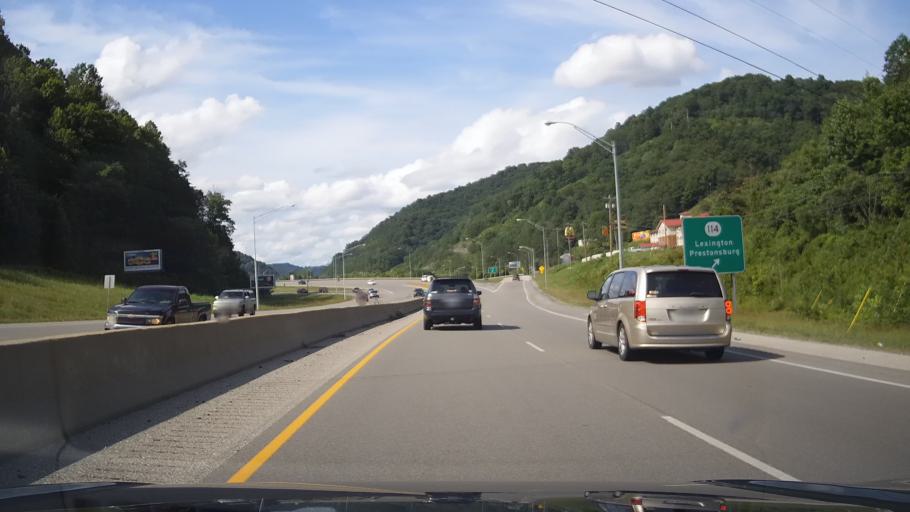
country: US
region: Kentucky
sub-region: Floyd County
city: Prestonsburg
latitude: 37.6535
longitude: -82.7853
